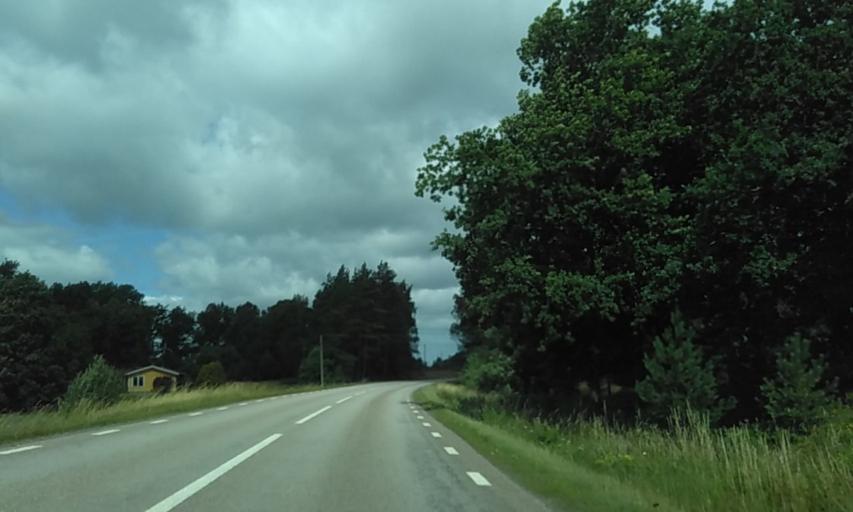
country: SE
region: Vaestra Goetaland
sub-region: Grastorps Kommun
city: Graestorp
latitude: 58.2690
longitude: 12.6820
